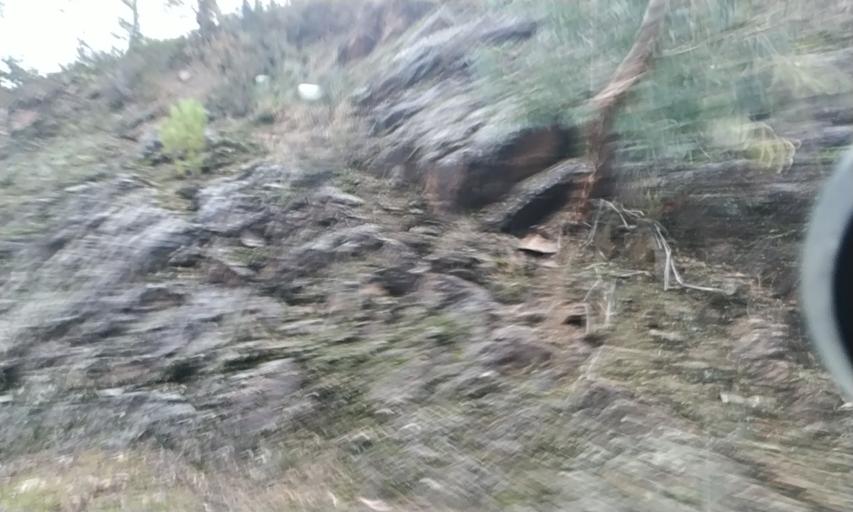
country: PT
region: Porto
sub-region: Amarante
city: Amarante
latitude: 41.3226
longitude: -8.0517
